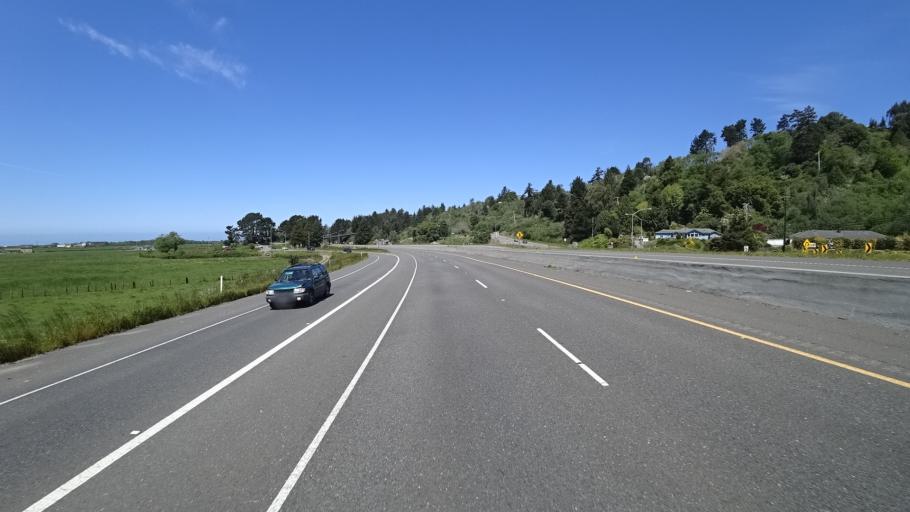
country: US
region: California
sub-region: Humboldt County
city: McKinleyville
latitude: 40.9185
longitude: -124.0947
